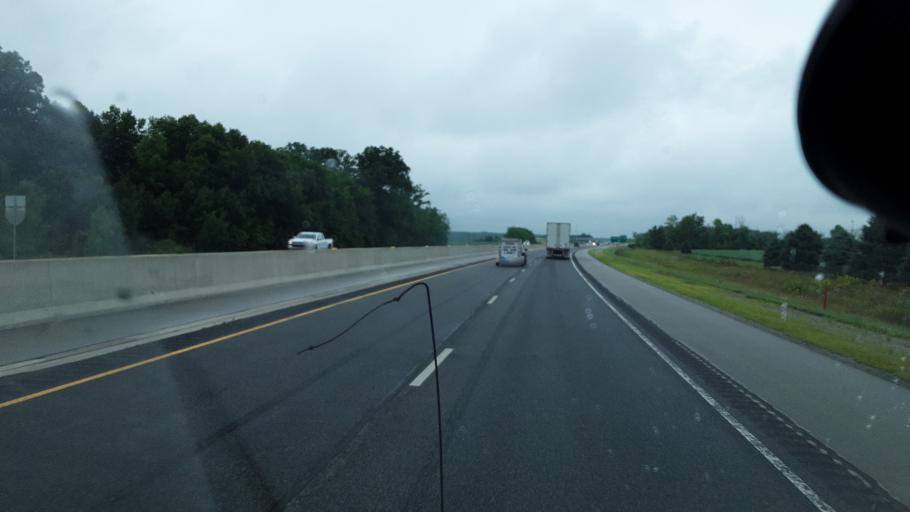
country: US
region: Indiana
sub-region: Wells County
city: Ossian
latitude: 40.9727
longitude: -85.1156
